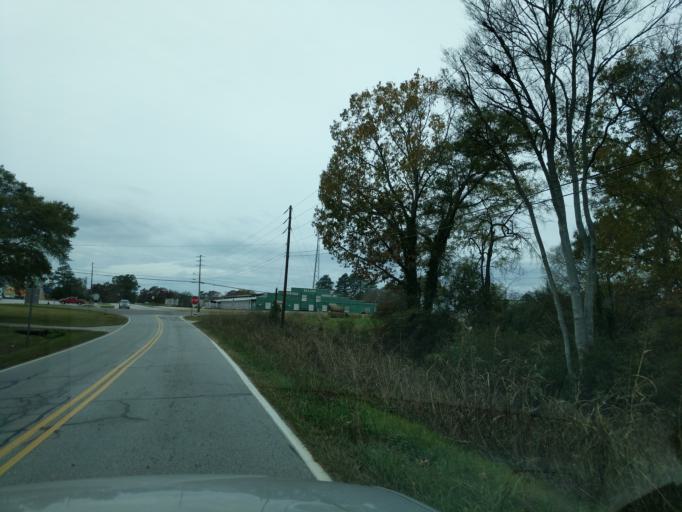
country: US
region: South Carolina
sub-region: Saluda County
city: Saluda
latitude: 34.0144
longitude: -81.7672
